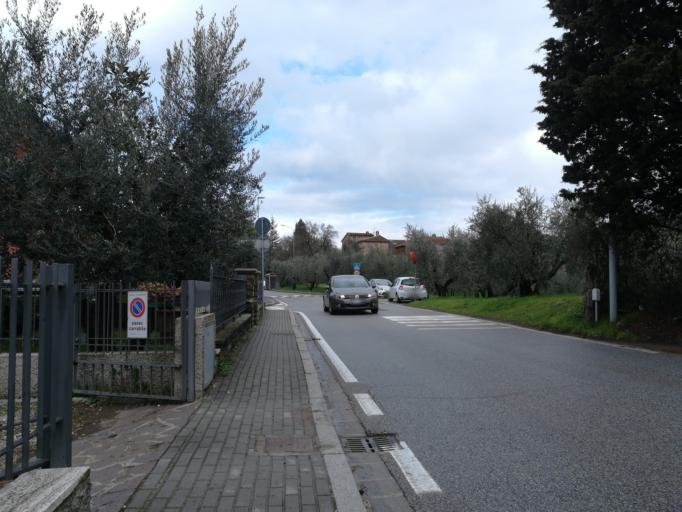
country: IT
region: Tuscany
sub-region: Provincia di Prato
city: Carmignano
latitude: 43.8026
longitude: 11.0319
